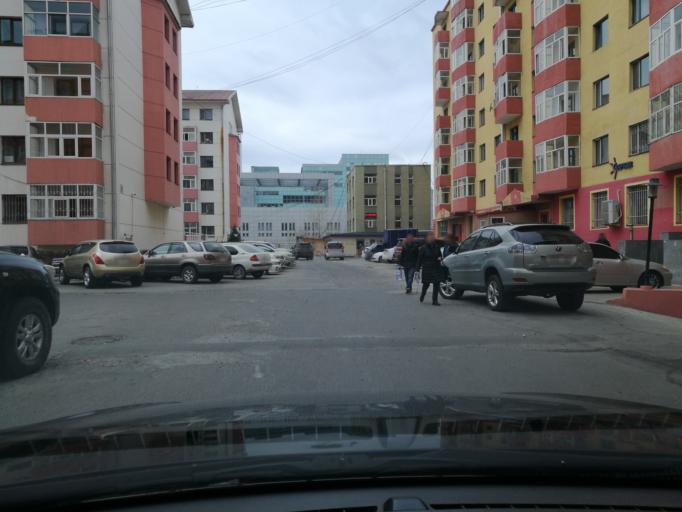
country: MN
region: Ulaanbaatar
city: Ulaanbaatar
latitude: 47.9040
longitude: 106.9257
